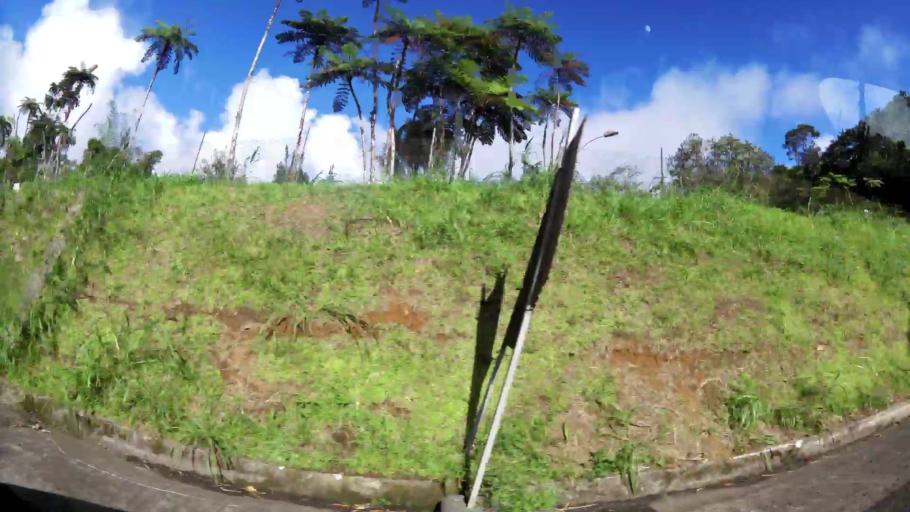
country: MQ
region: Martinique
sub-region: Martinique
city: Saint-Joseph
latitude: 14.6891
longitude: -61.0862
